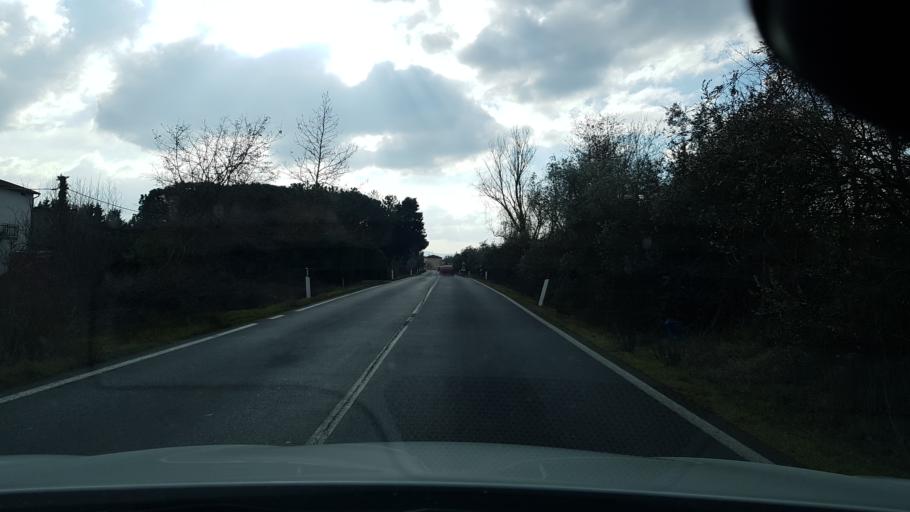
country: IT
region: Umbria
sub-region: Provincia di Perugia
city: Castiglione del Lago
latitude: 43.1571
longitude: 12.0177
